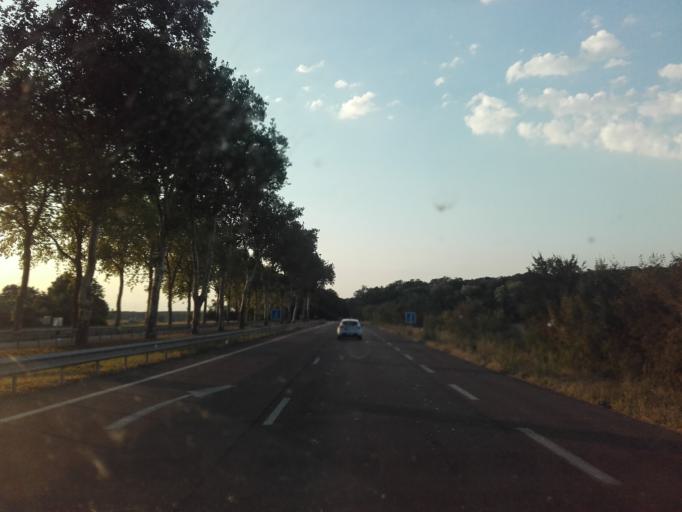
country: FR
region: Bourgogne
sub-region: Departement de l'Yonne
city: Auxerre
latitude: 47.8261
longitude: 3.5557
